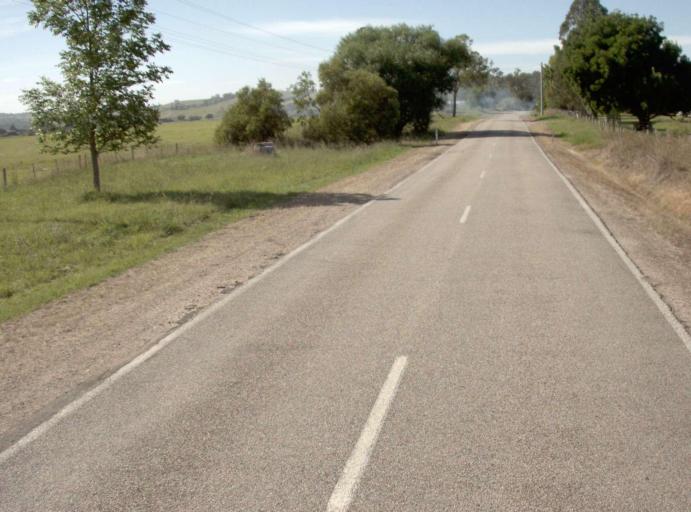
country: AU
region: Victoria
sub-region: East Gippsland
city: Bairnsdale
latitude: -37.7300
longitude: 147.8098
